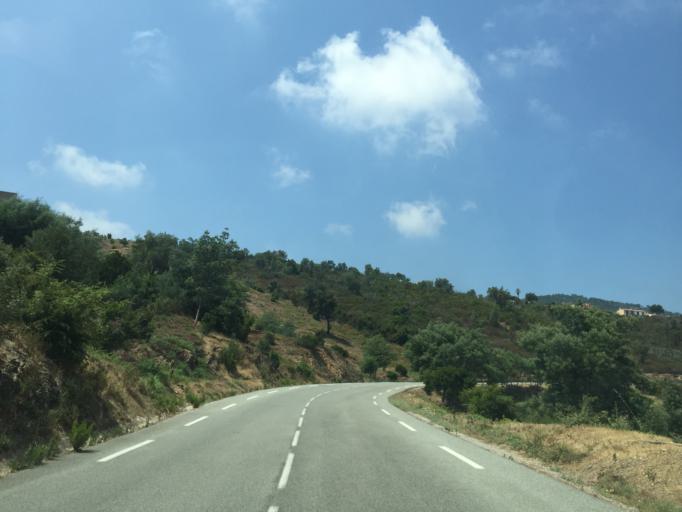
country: FR
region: Provence-Alpes-Cote d'Azur
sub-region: Departement du Var
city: Sainte-Maxime
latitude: 43.3508
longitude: 6.6751
